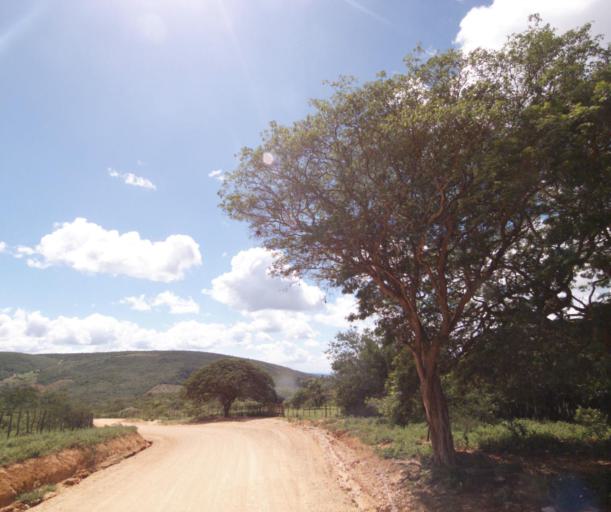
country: BR
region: Bahia
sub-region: Pocoes
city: Pocoes
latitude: -14.2986
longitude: -40.6775
